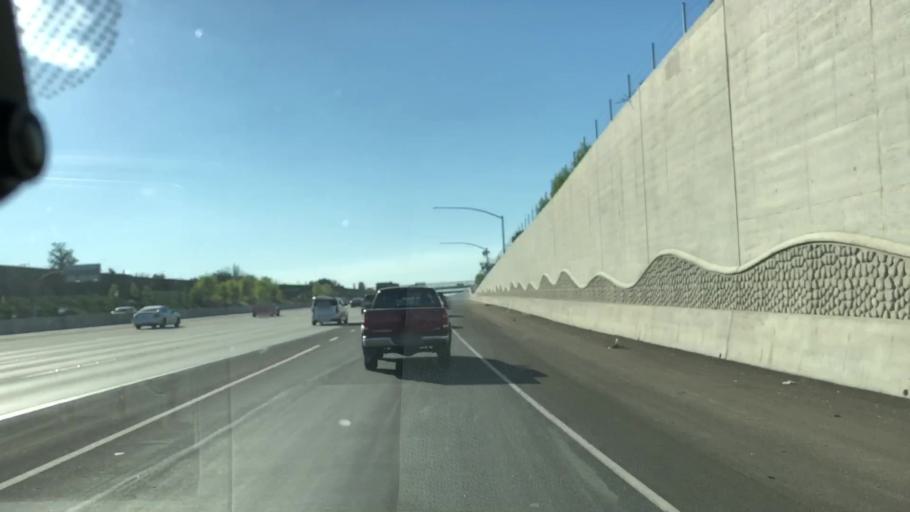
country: US
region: California
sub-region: San Bernardino County
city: Rialto
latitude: 34.1361
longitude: -117.3741
